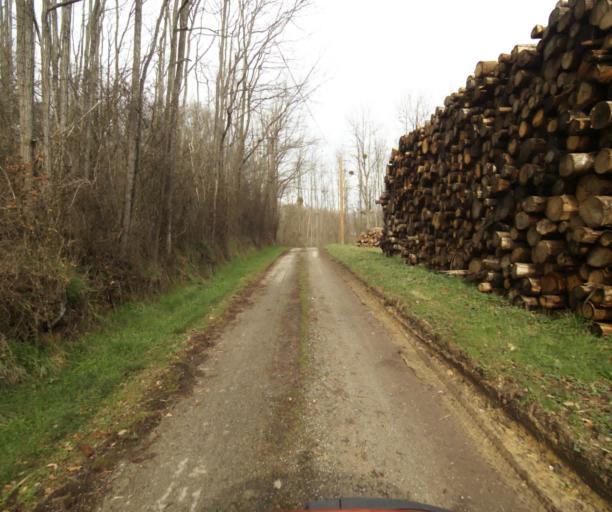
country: FR
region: Midi-Pyrenees
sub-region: Departement de l'Ariege
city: Verniolle
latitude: 43.0761
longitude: 1.7080
